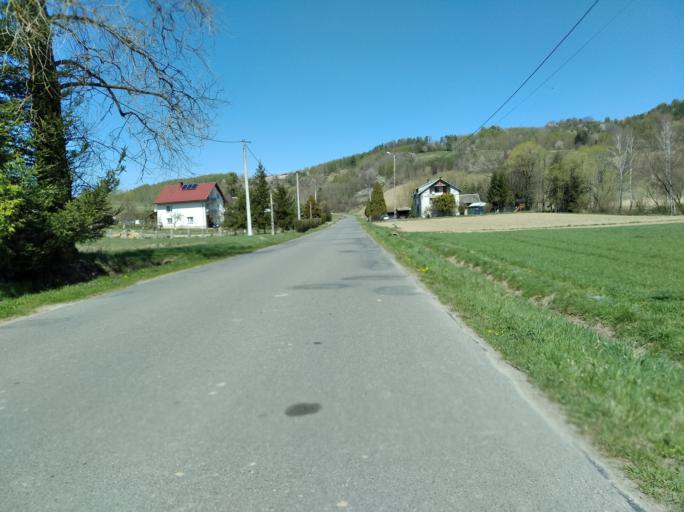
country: PL
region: Subcarpathian Voivodeship
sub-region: Powiat brzozowski
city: Dydnia
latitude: 49.6997
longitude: 22.1523
